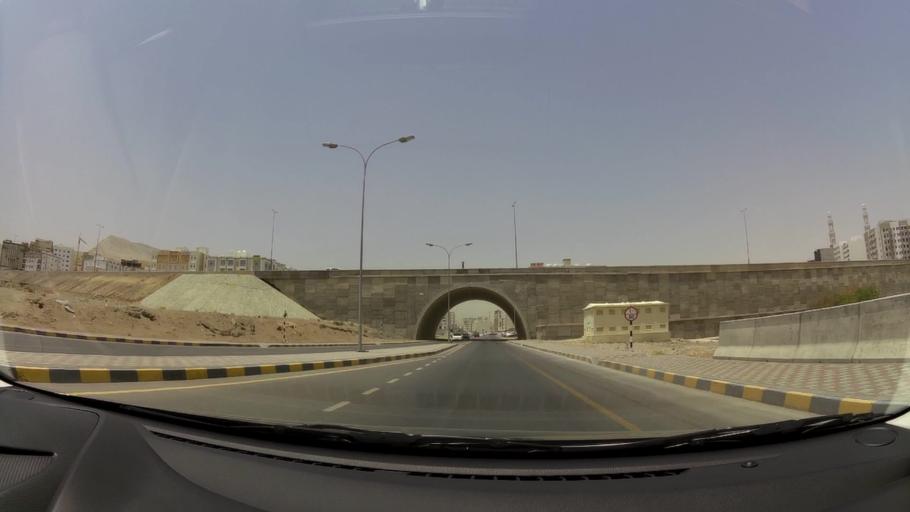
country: OM
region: Muhafazat Masqat
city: Bawshar
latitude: 23.5788
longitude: 58.4198
